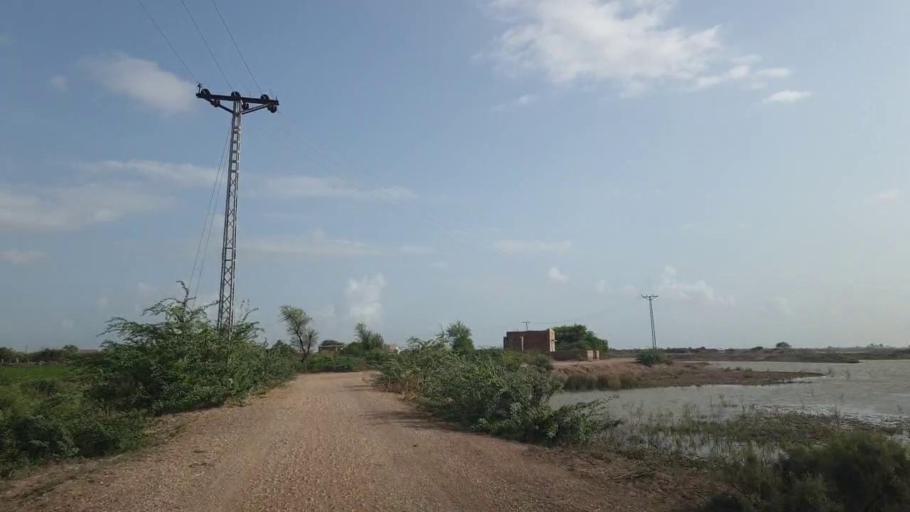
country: PK
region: Sindh
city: Kadhan
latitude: 24.6342
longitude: 69.0811
